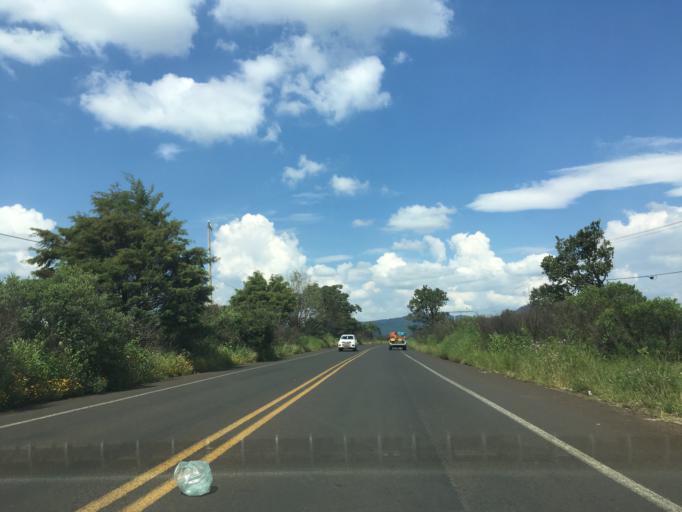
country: MX
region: Michoacan
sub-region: Tingueindin
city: Tingueindin
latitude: 19.8213
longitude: -102.5093
